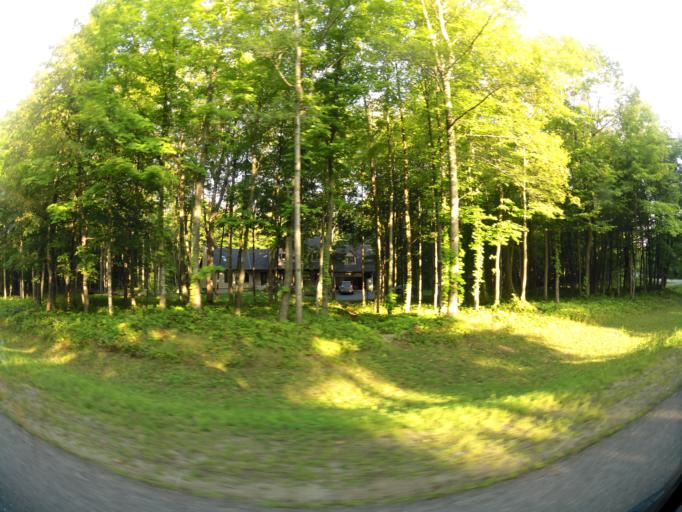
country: CA
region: Ontario
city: Clarence-Rockland
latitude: 45.5067
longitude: -75.4109
